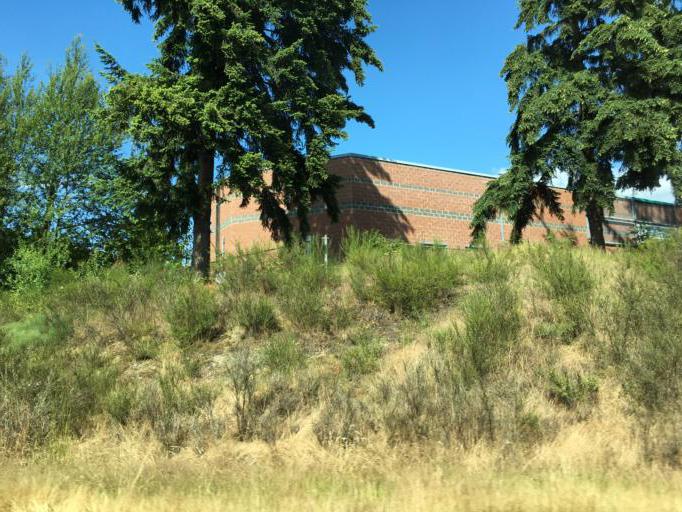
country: US
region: Washington
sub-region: Snohomish County
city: Mountlake Terrace
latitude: 47.7780
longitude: -122.3154
